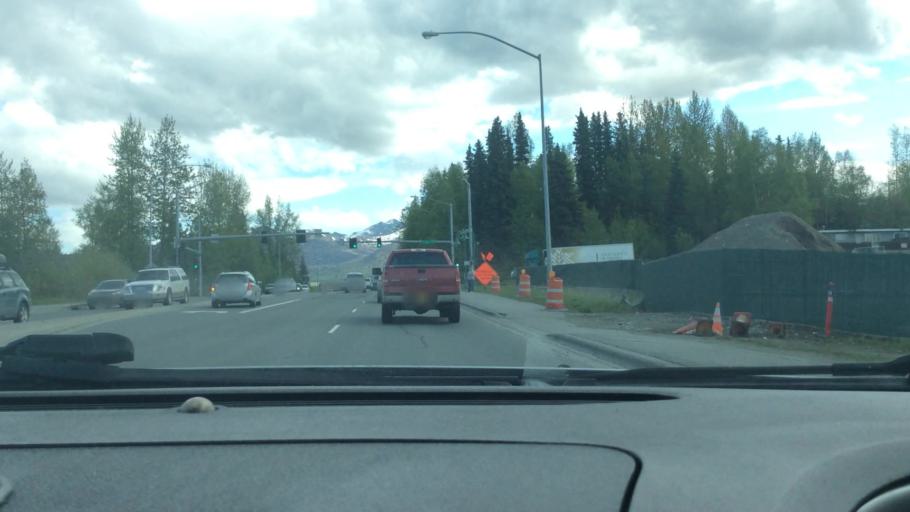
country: US
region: Alaska
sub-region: Anchorage Municipality
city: Anchorage
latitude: 61.1808
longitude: -149.8254
